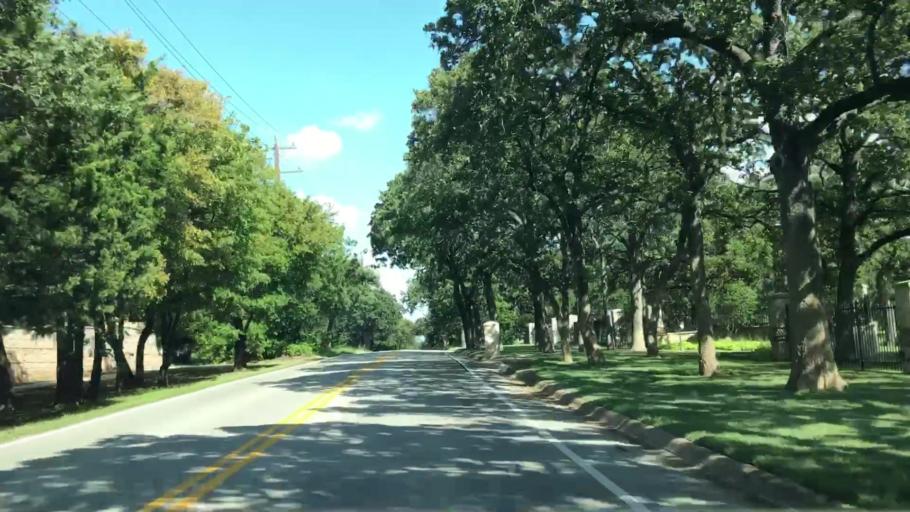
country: US
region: Texas
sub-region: Tarrant County
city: Keller
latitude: 32.9076
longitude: -97.2233
